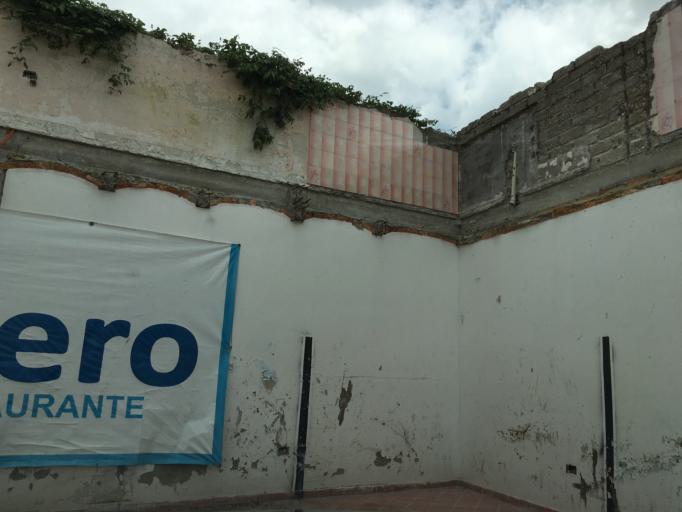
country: MX
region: Nayarit
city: Xalisco
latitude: 21.4705
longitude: -104.8873
